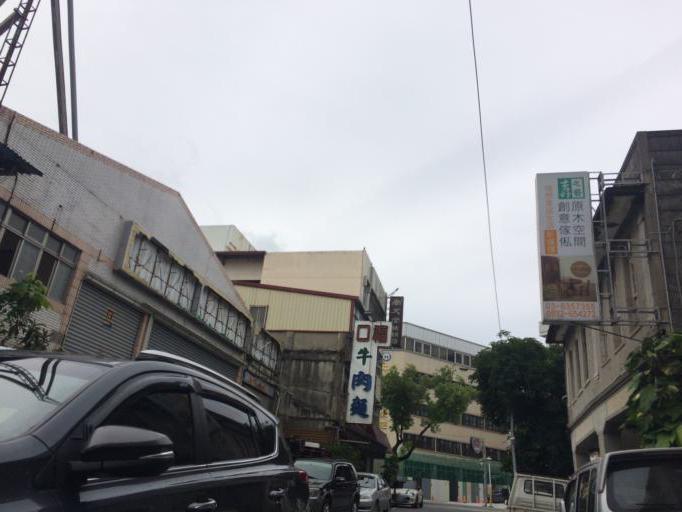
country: TW
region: Taiwan
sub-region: Hualien
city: Hualian
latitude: 23.9760
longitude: 121.6114
